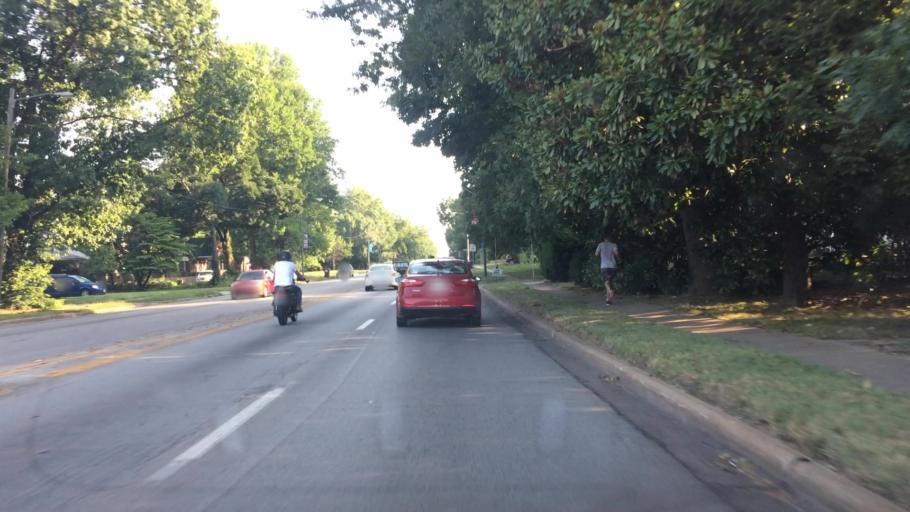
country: US
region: Missouri
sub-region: Greene County
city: Springfield
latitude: 37.1895
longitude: -93.2764
